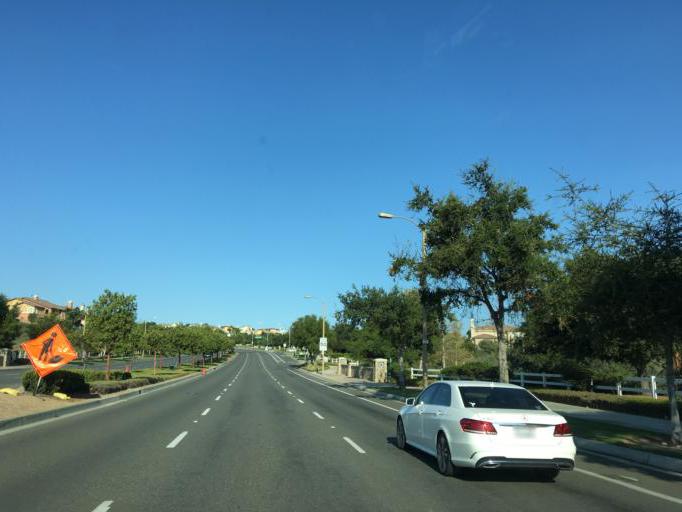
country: US
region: California
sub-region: Los Angeles County
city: Santa Clarita
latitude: 34.4075
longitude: -118.5805
